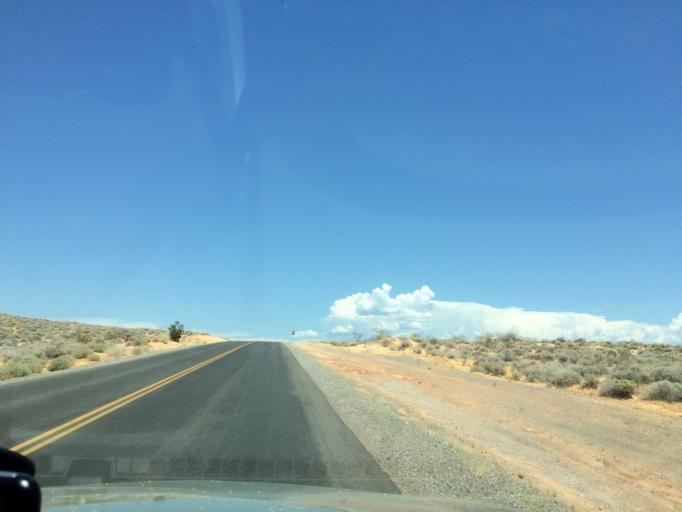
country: US
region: Nevada
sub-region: Clark County
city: Moapa Valley
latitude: 36.4531
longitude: -114.5127
